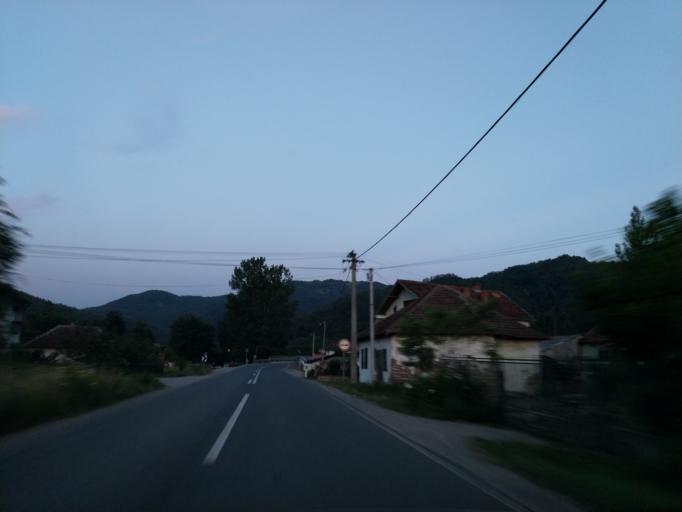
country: RS
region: Central Serbia
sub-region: Rasinski Okrug
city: Aleksandrovac
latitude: 43.3515
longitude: 21.0802
